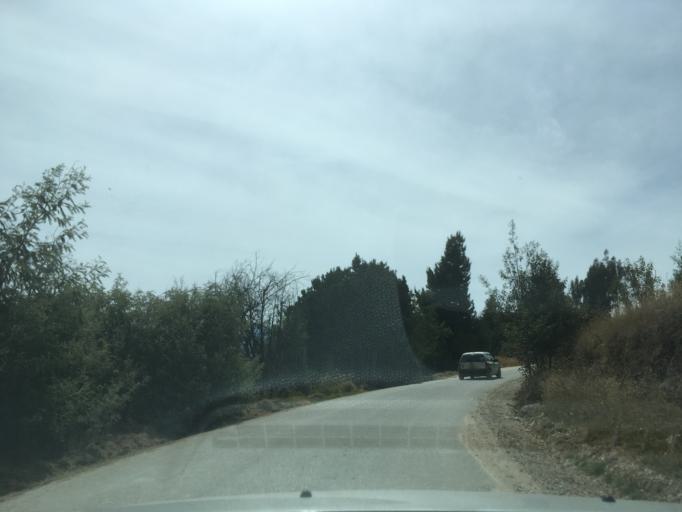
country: CO
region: Boyaca
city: Aquitania
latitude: 5.5844
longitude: -72.9242
